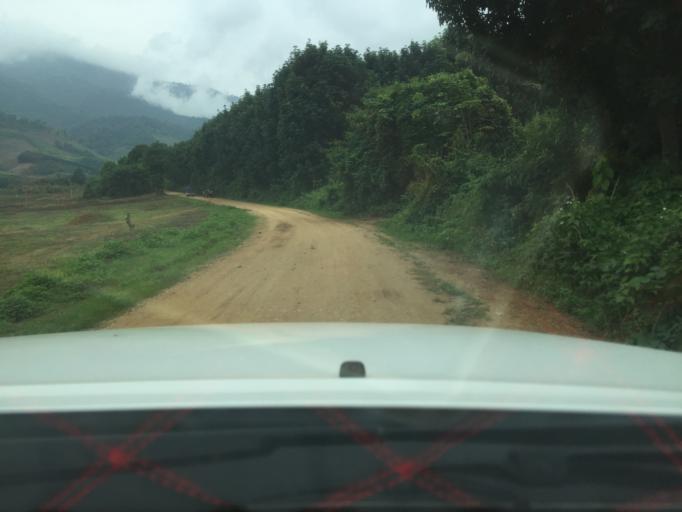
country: TH
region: Phayao
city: Phu Sang
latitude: 19.7418
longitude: 100.4457
